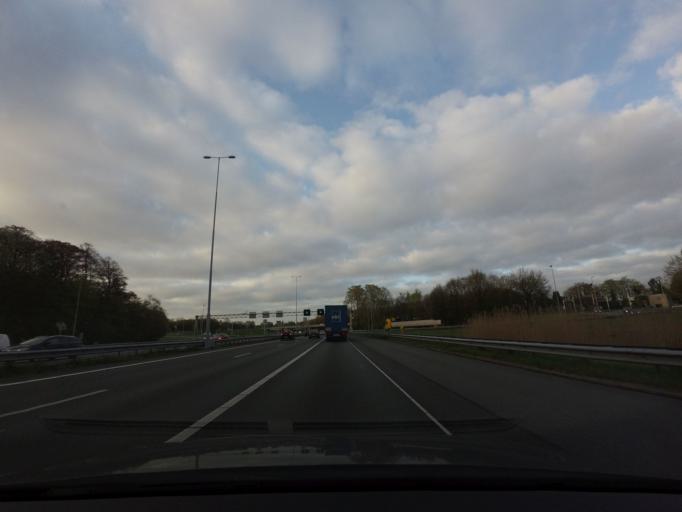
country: NL
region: North Holland
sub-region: Gemeente Bussum
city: Bussum
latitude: 52.2824
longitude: 5.1836
